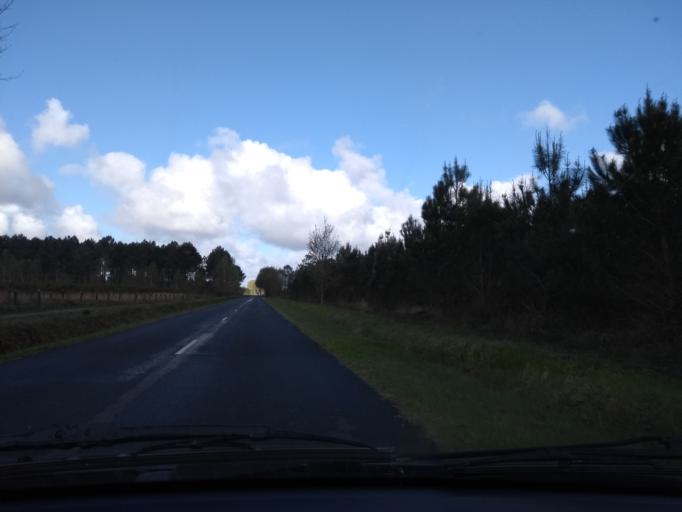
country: FR
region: Aquitaine
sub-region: Departement de la Gironde
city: Mios
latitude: 44.5500
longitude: -0.9767
